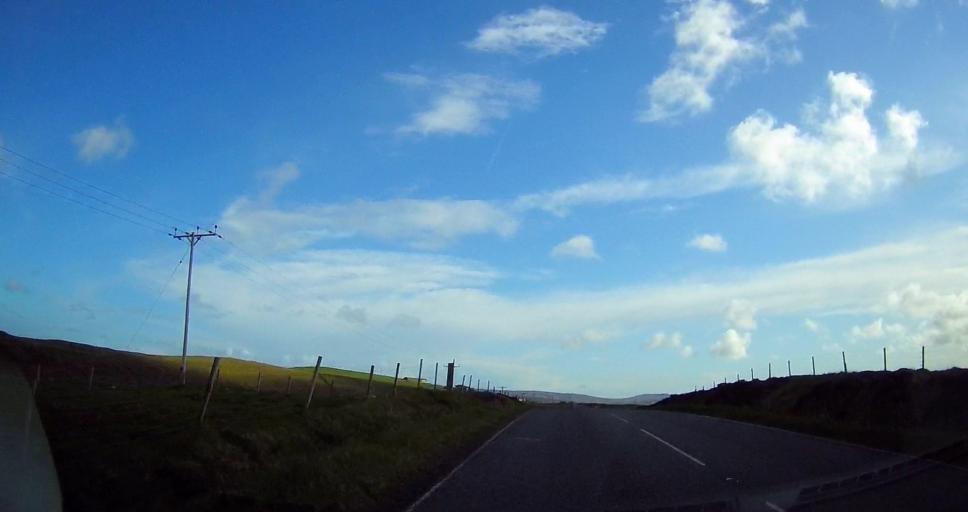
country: GB
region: Scotland
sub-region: Shetland Islands
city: Shetland
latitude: 60.3626
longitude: -1.1427
